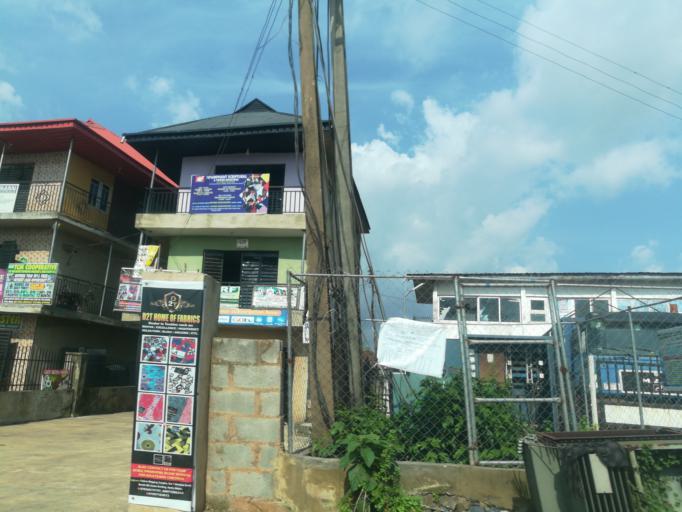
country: NG
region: Oyo
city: Ibadan
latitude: 7.3864
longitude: 3.8239
